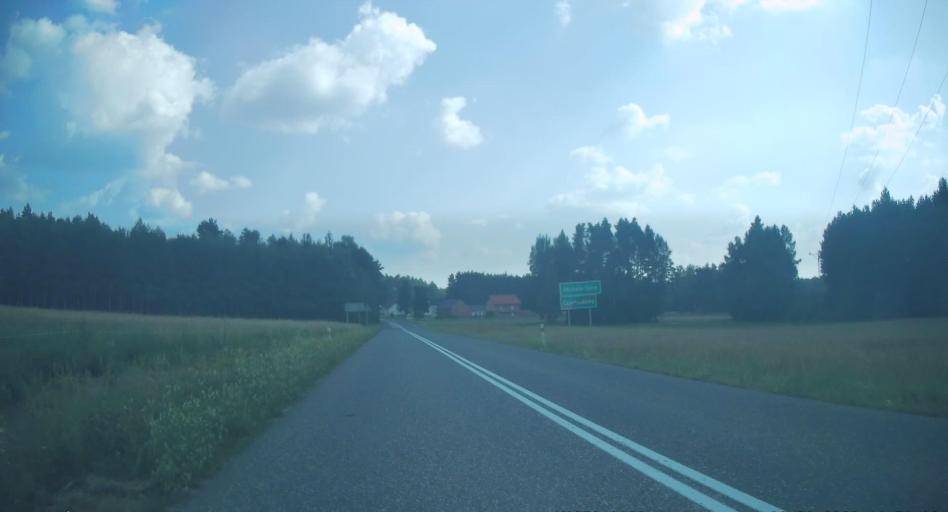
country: PL
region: Swietokrzyskie
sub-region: Powiat kielecki
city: Lopuszno
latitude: 50.8989
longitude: 20.2494
